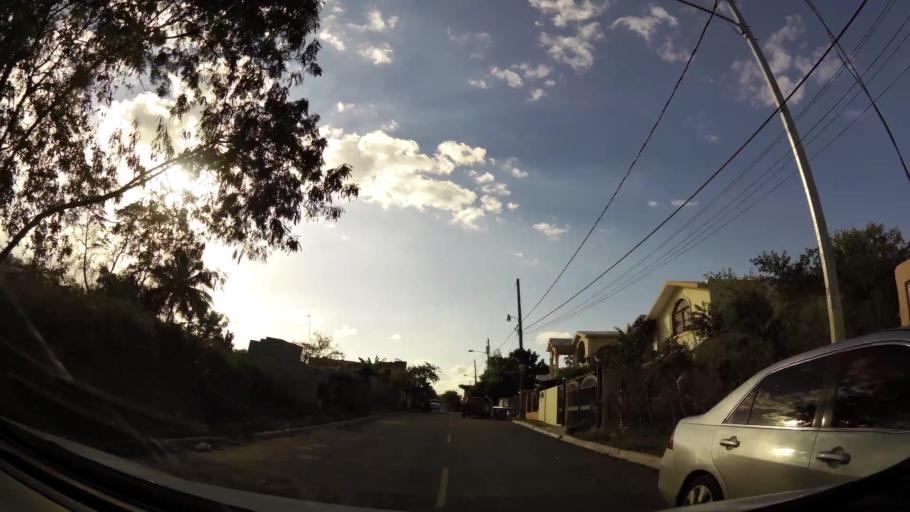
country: DO
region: Nacional
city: Ensanche Luperon
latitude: 18.5472
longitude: -69.9122
